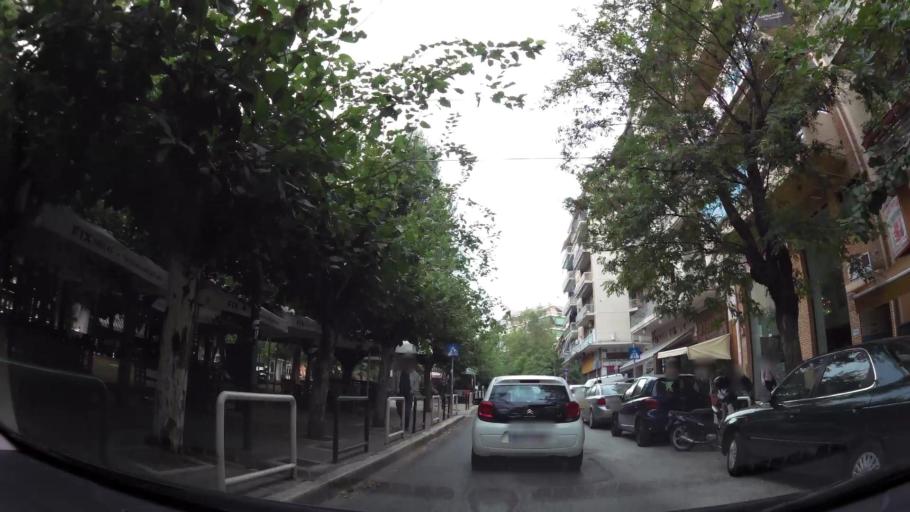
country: GR
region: Attica
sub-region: Nomarchia Athinas
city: Kipseli
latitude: 37.9929
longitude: 23.7492
